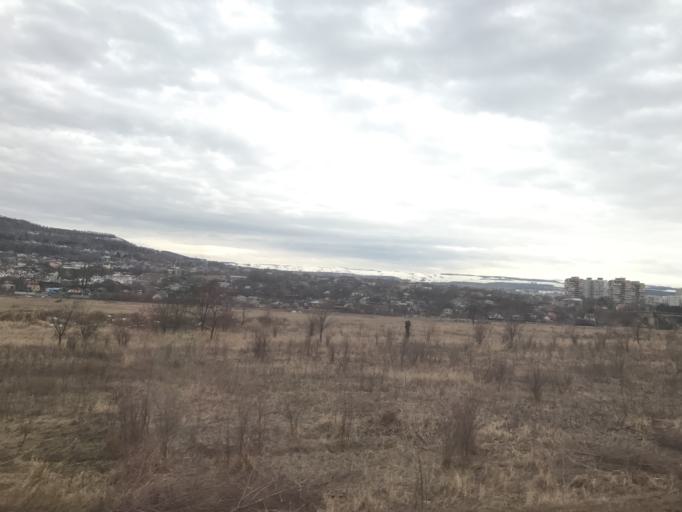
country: RU
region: Stavropol'skiy
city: Kislovodsk
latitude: 43.9472
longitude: 42.7363
